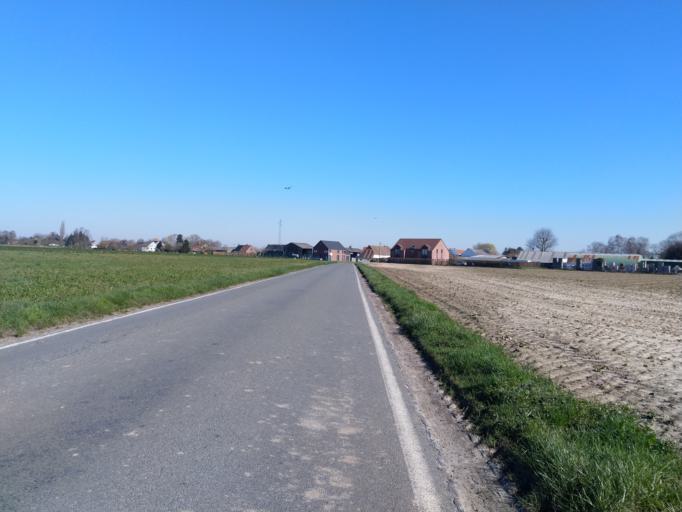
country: BE
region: Wallonia
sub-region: Province du Hainaut
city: Lens
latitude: 50.5420
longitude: 3.8582
